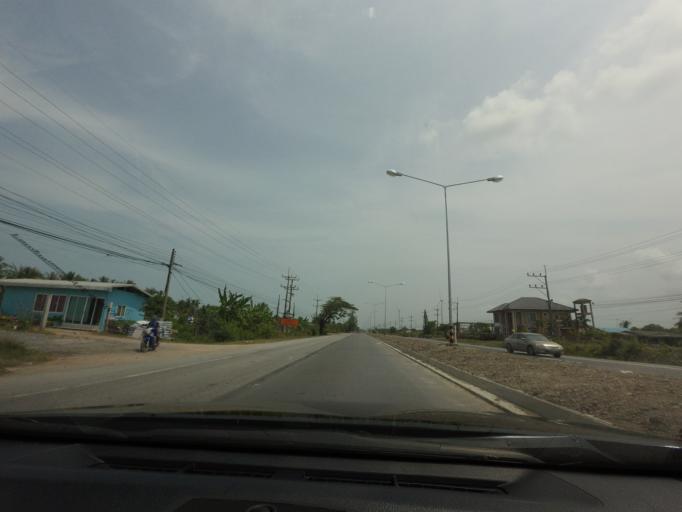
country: TH
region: Songkhla
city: Ranot
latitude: 7.8780
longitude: 100.3458
